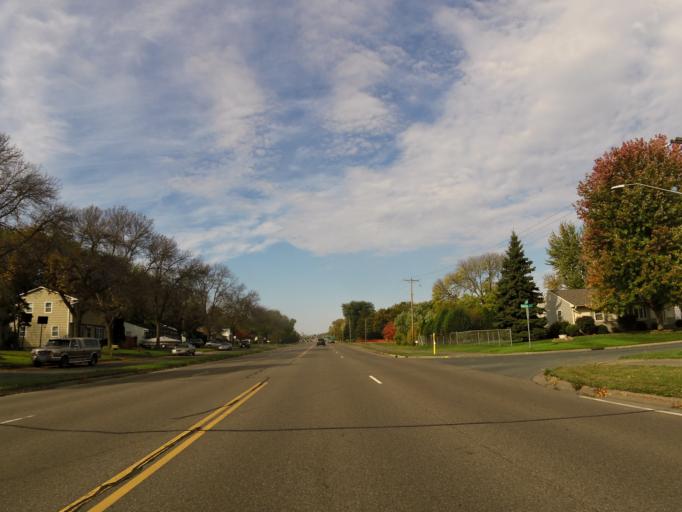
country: US
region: Minnesota
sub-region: Dakota County
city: Eagan
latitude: 44.8047
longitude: -93.2108
